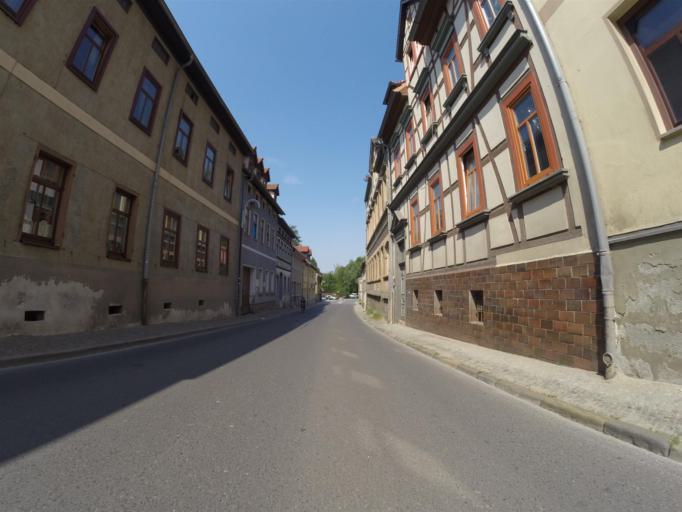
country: DE
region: Thuringia
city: Stadtroda
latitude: 50.8614
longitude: 11.7236
